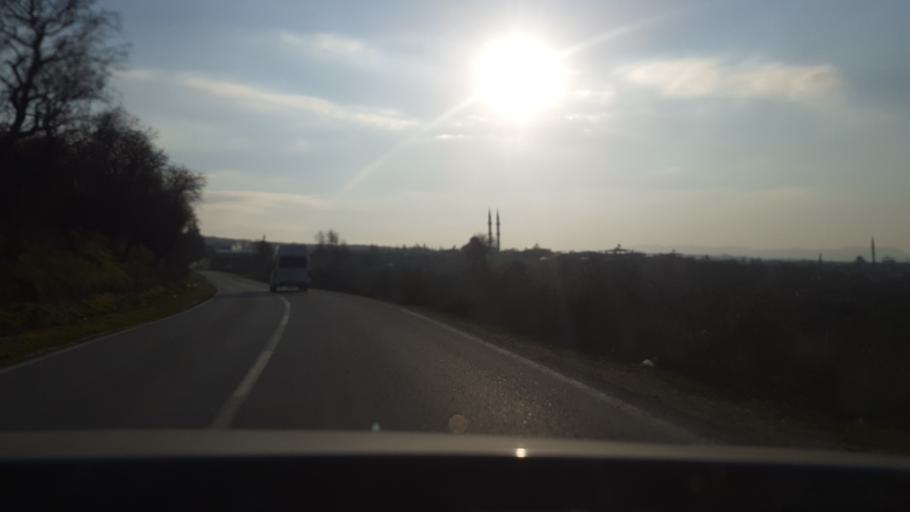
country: TR
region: Hatay
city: Oymakli
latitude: 36.1153
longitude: 36.3024
